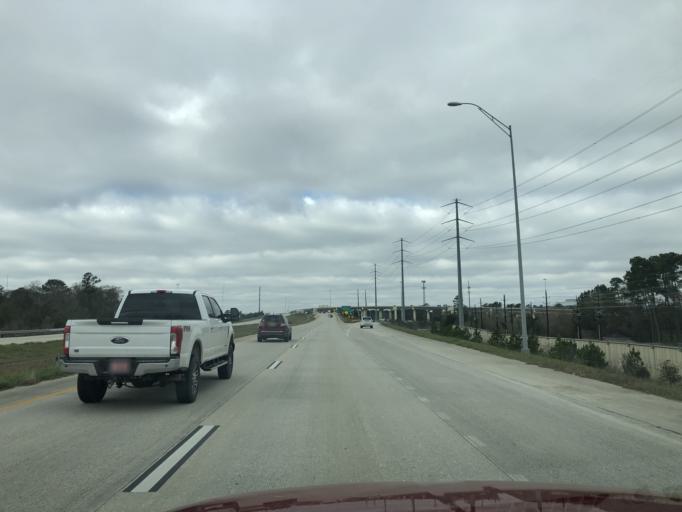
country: US
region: Texas
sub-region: Harris County
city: Spring
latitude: 30.0925
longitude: -95.4287
